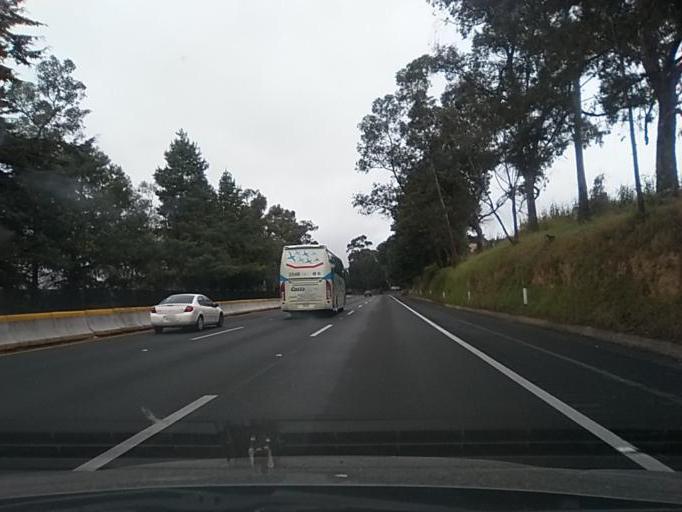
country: MX
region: Mexico City
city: Xochimilco
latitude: 19.1817
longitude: -99.1555
